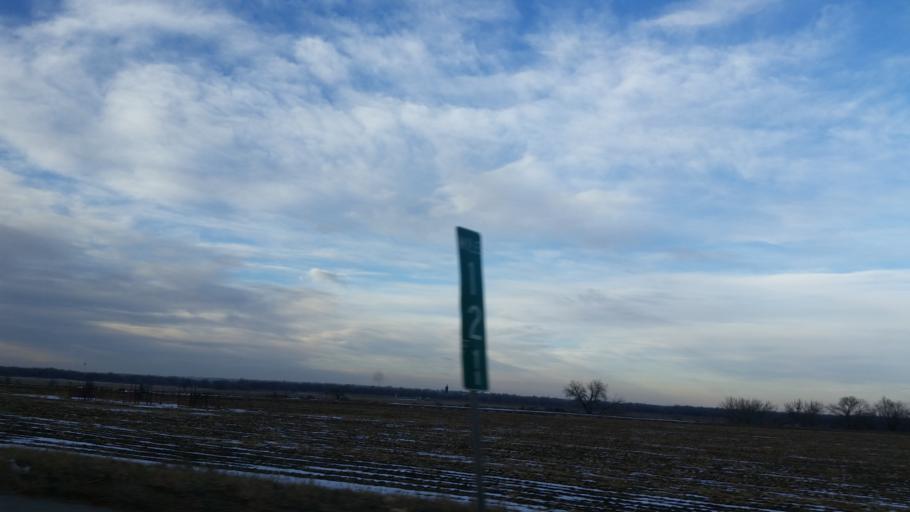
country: US
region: Colorado
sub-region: Weld County
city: Kersey
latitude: 40.3863
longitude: -104.5330
